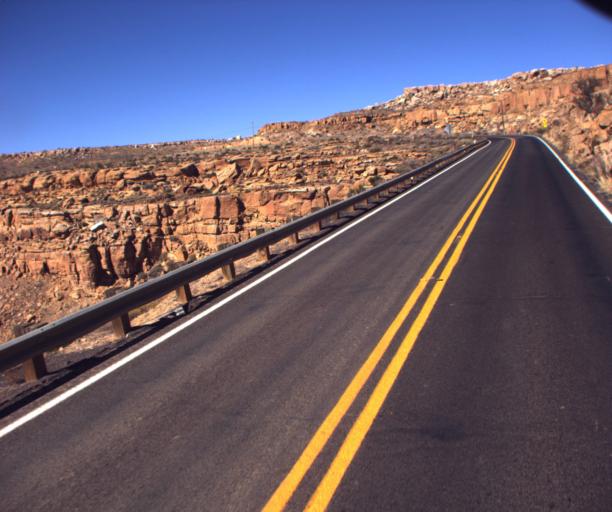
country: US
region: Arizona
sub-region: Navajo County
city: First Mesa
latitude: 35.8839
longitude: -110.6286
